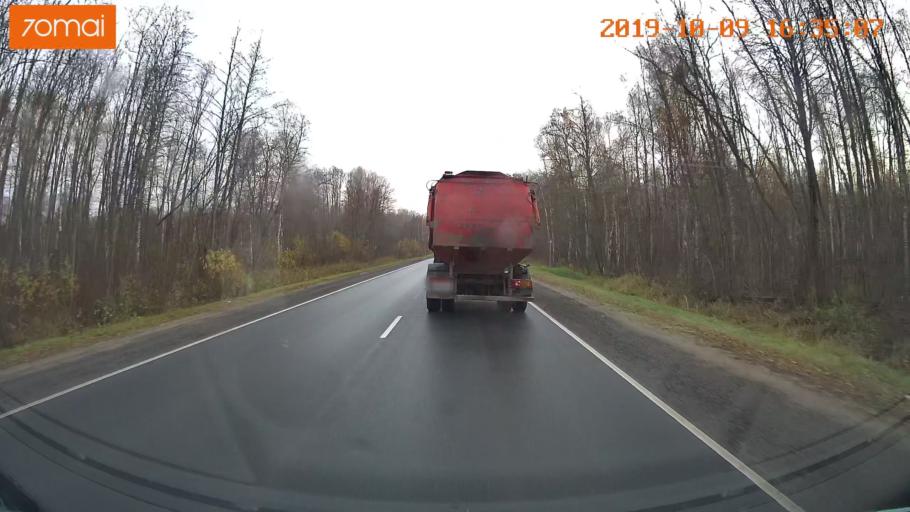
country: RU
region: Kostroma
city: Oktyabr'skiy
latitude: 57.5591
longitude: 40.9979
